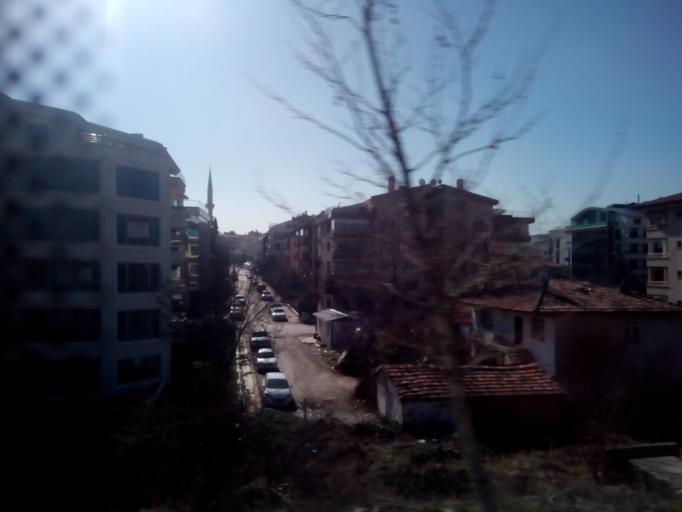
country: TR
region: Ankara
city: Batikent
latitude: 39.9166
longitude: 32.7691
